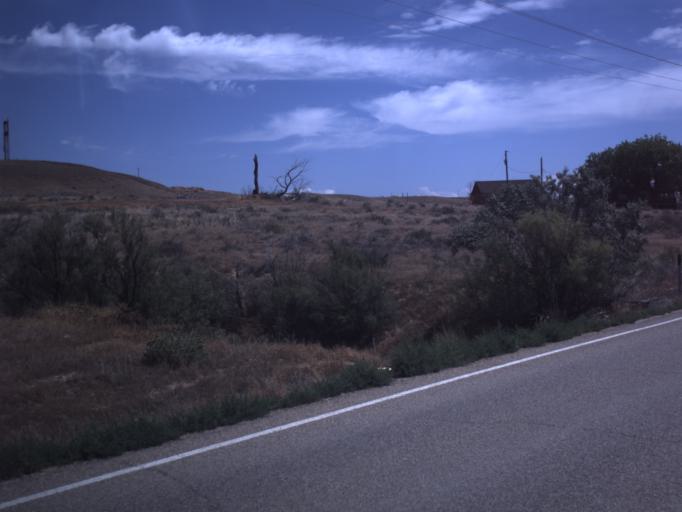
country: US
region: Utah
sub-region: Uintah County
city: Naples
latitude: 40.2127
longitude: -109.6715
